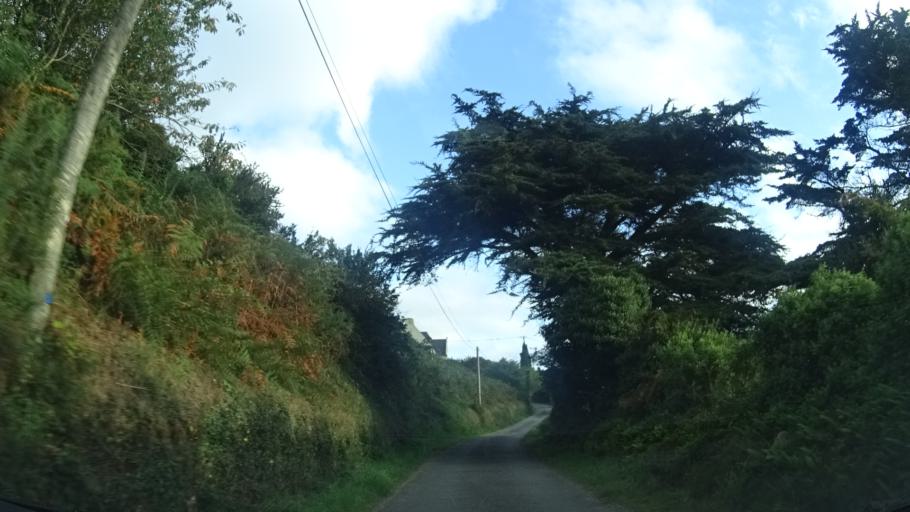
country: FR
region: Brittany
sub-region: Departement du Finistere
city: Lampaul-Plouarzel
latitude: 48.4604
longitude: -4.7603
